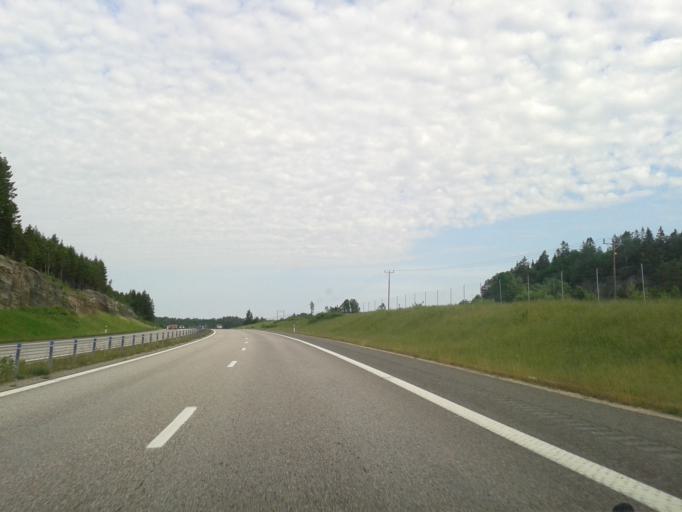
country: SE
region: Vaestra Goetaland
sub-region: Munkedals Kommun
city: Munkedal
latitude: 58.4734
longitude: 11.6456
